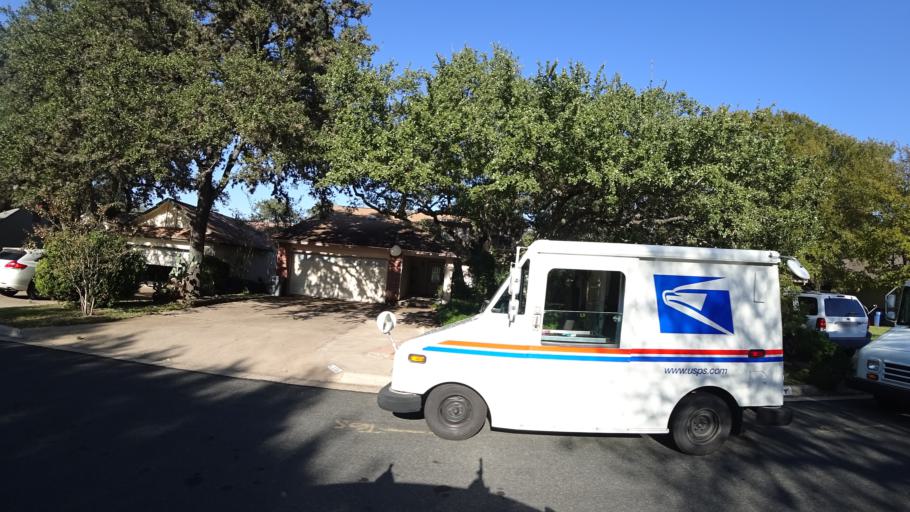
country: US
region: Texas
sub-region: Travis County
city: Shady Hollow
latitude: 30.2113
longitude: -97.8464
